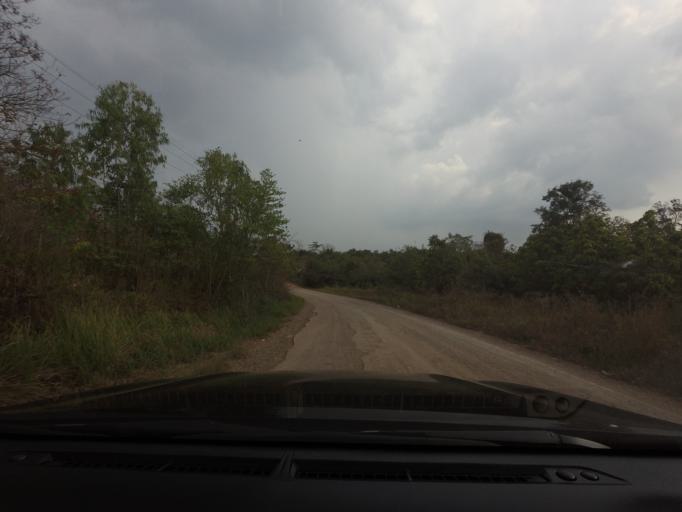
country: TH
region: Nakhon Ratchasima
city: Wang Nam Khiao
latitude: 14.4417
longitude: 101.6920
